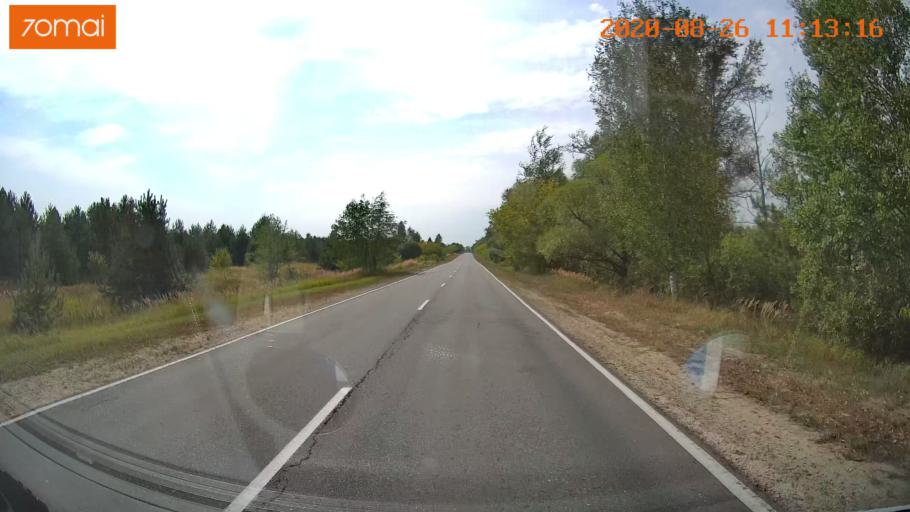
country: RU
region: Rjazan
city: Izhevskoye
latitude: 54.4600
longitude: 41.1216
